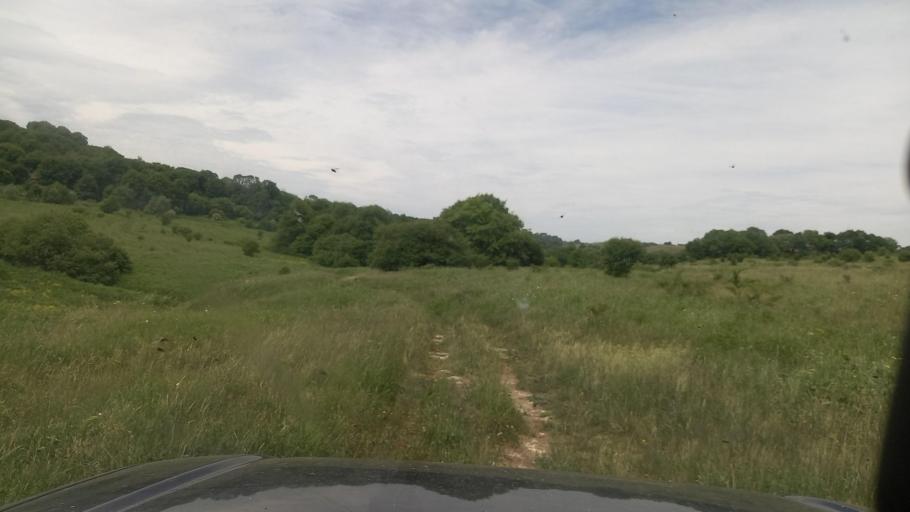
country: RU
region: Karachayevo-Cherkesiya
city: Pregradnaya
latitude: 44.0926
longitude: 41.1750
